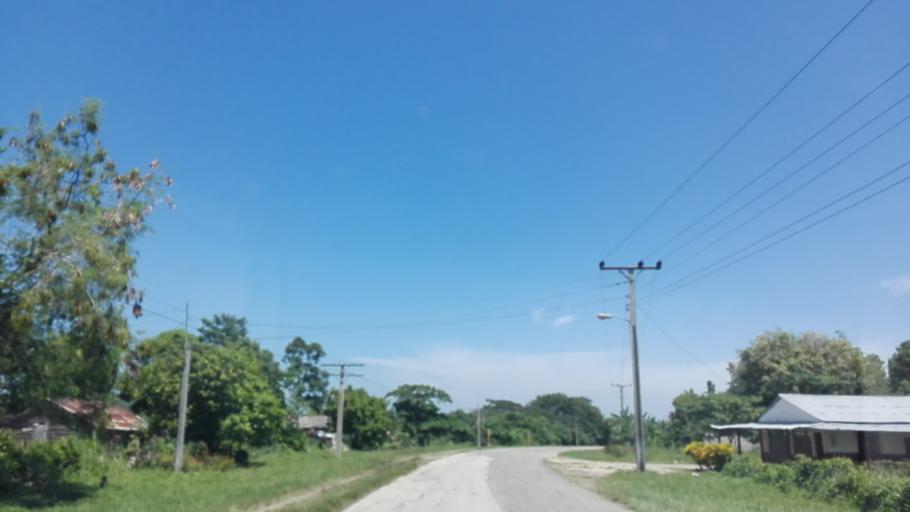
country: CU
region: Granma
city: Bartolome Maso
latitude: 20.1431
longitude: -76.9474
